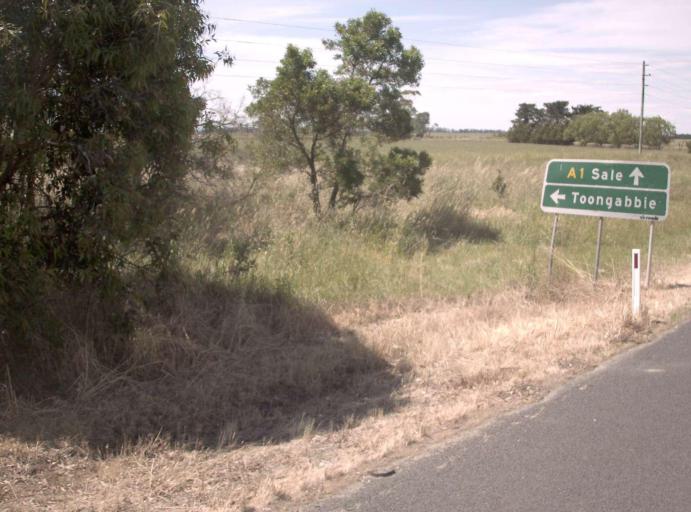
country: AU
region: Victoria
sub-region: Wellington
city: Heyfield
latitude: -38.1086
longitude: 146.8940
